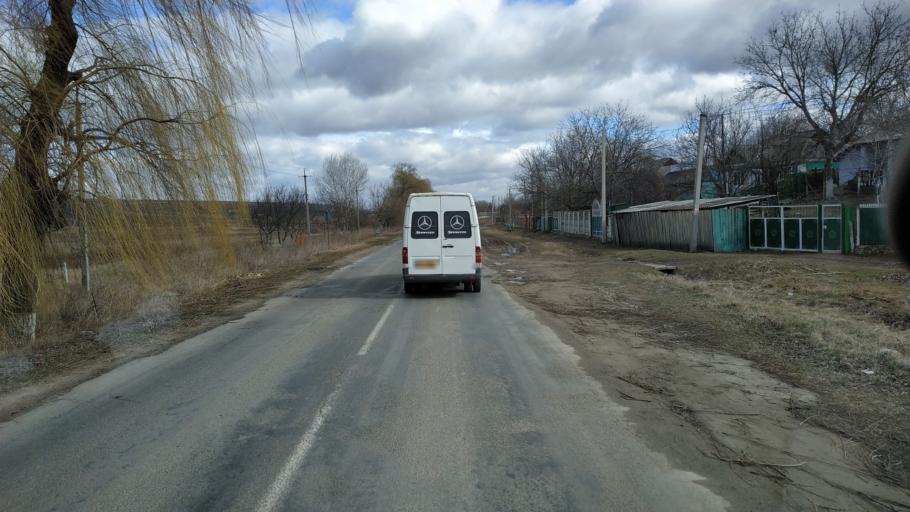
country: MD
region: Stinga Nistrului
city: Bucovat
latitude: 47.1457
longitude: 28.3955
